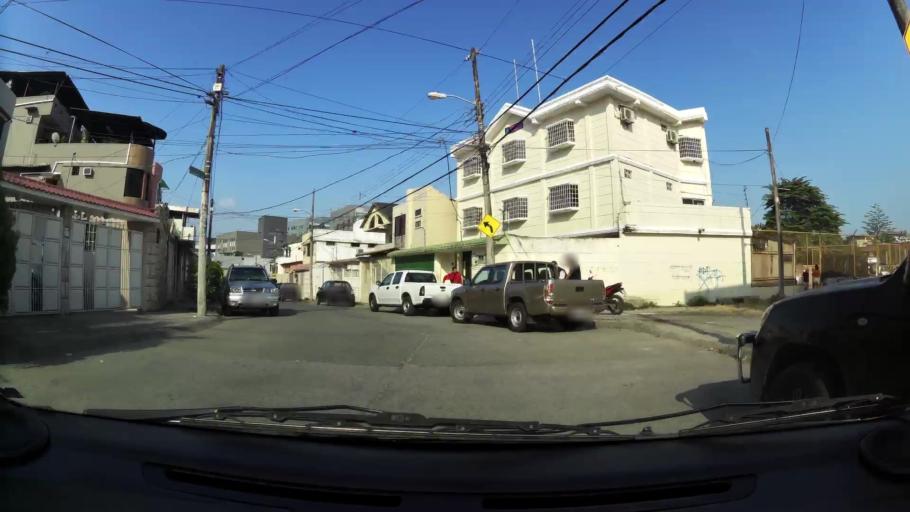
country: EC
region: Guayas
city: Guayaquil
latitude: -2.1508
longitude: -79.9090
